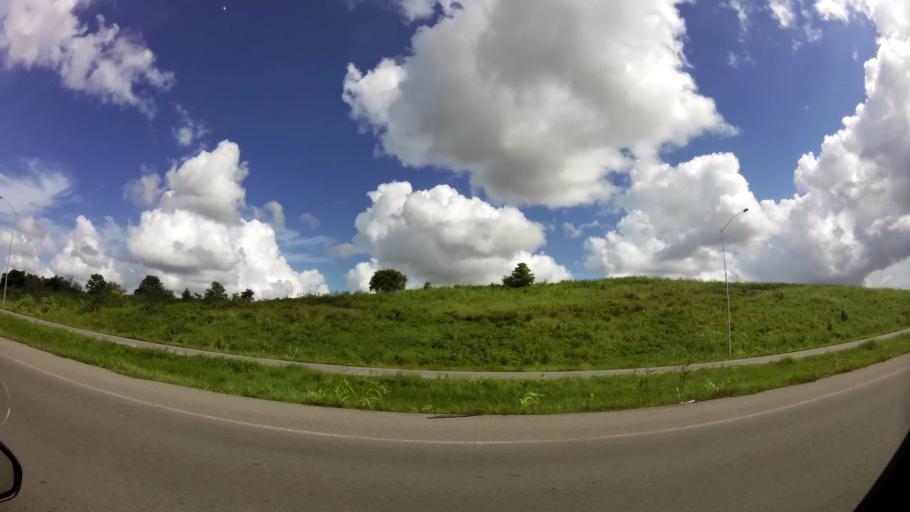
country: TT
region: Penal/Debe
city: Debe
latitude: 10.2326
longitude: -61.4477
